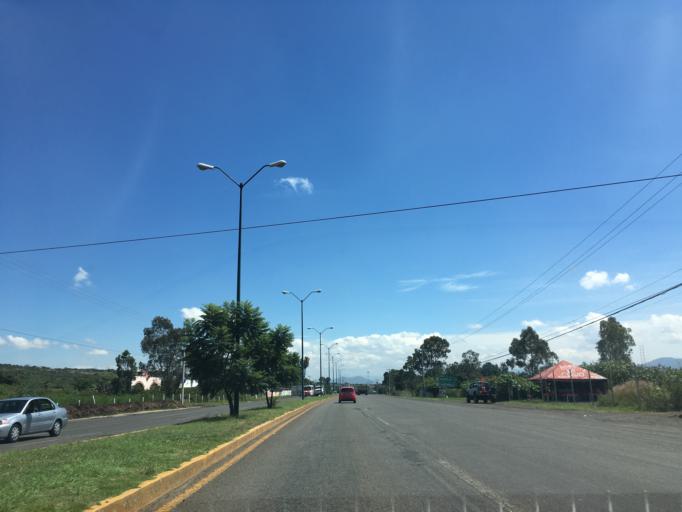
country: MX
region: Michoacan
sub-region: Morelia
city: Conjunto Habitacional Villas del Pedregal
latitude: 19.6870
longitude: -101.3134
